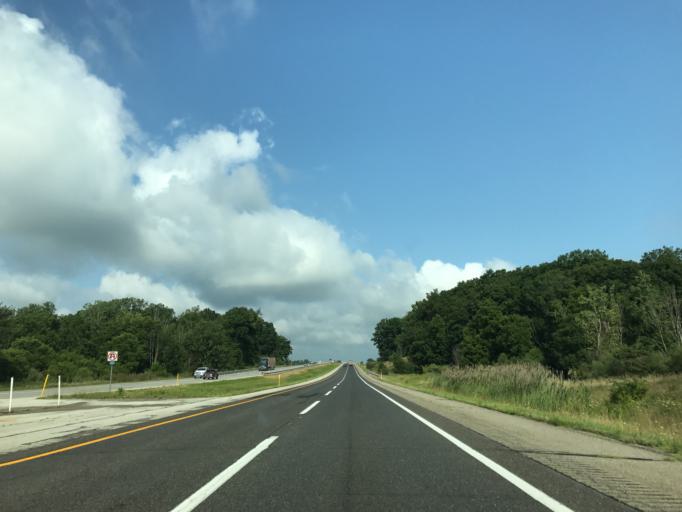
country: US
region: Indiana
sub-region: Steuben County
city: Fremont
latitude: 41.7079
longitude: -84.9333
